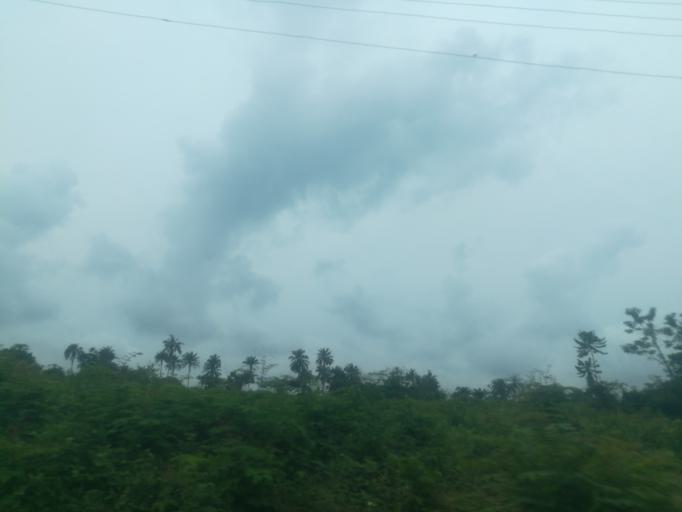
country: NG
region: Ogun
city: Ayetoro
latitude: 7.1114
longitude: 3.1280
